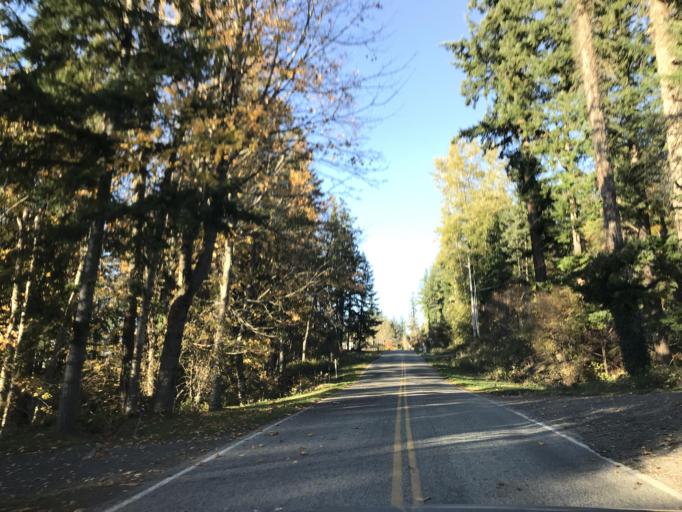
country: US
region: Washington
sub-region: Whatcom County
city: Geneva
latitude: 48.7756
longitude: -122.3991
